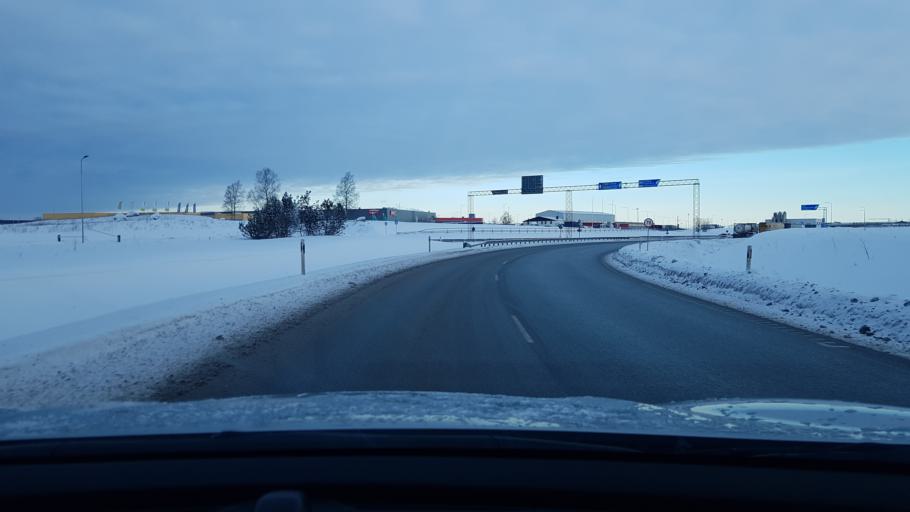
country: EE
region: Harju
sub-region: Rae vald
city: Jueri
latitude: 59.3544
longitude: 24.8856
